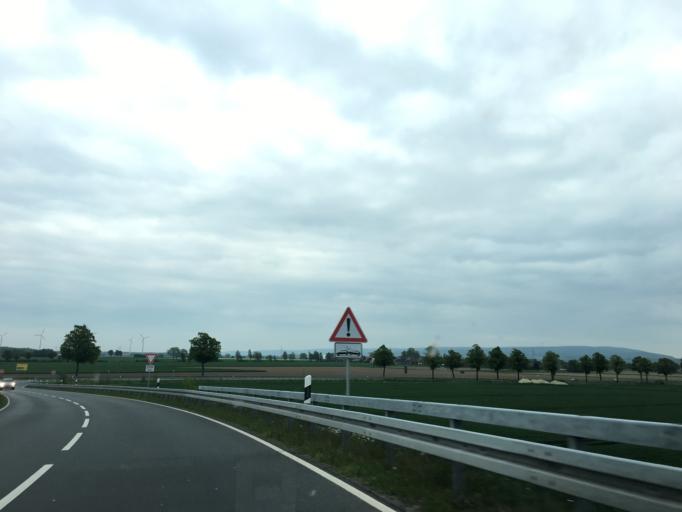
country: DE
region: Lower Saxony
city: Hohnhorst
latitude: 52.3739
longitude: 9.3824
